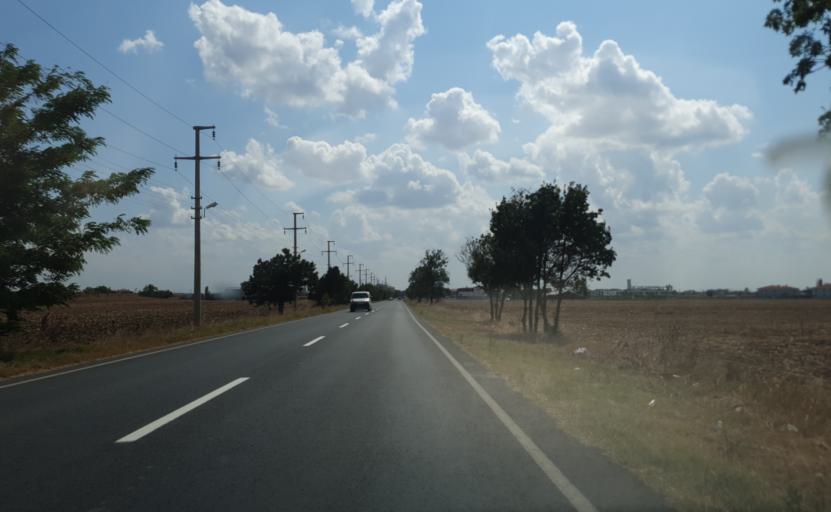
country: TR
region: Kirklareli
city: Luleburgaz
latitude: 41.3690
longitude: 27.3395
